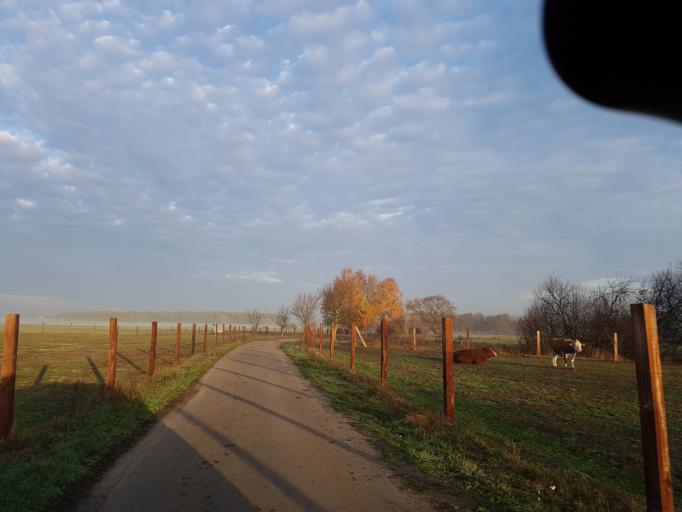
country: DE
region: Saxony-Anhalt
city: Elster
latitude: 51.8792
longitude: 12.8471
